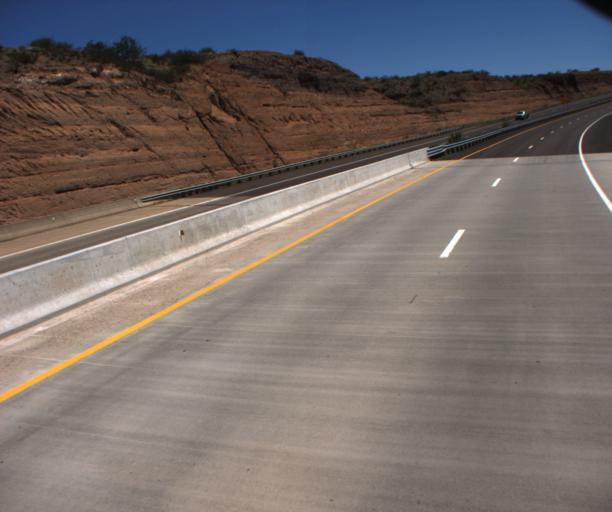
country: US
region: Arizona
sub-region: Greenlee County
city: Clifton
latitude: 32.9541
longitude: -109.2296
